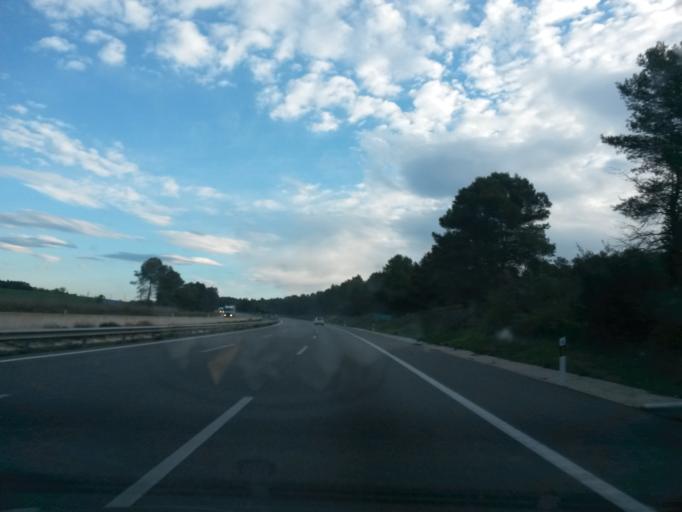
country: ES
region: Catalonia
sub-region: Provincia de Girona
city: Viladasens
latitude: 42.1096
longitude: 2.9125
